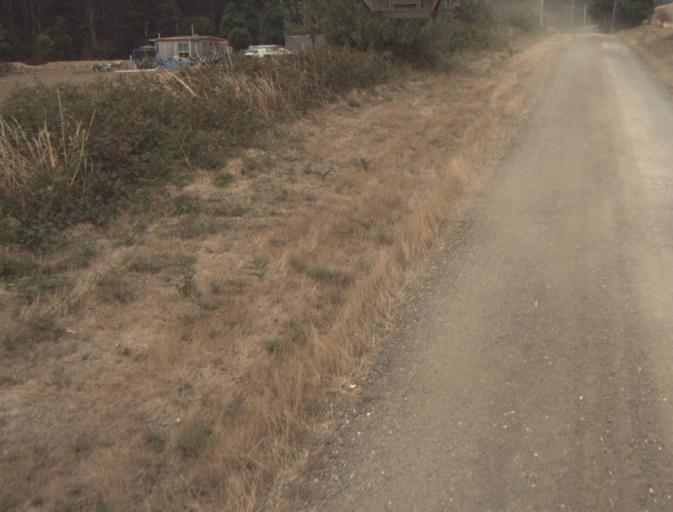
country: AU
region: Tasmania
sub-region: Dorset
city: Bridport
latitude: -41.1829
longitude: 147.2617
